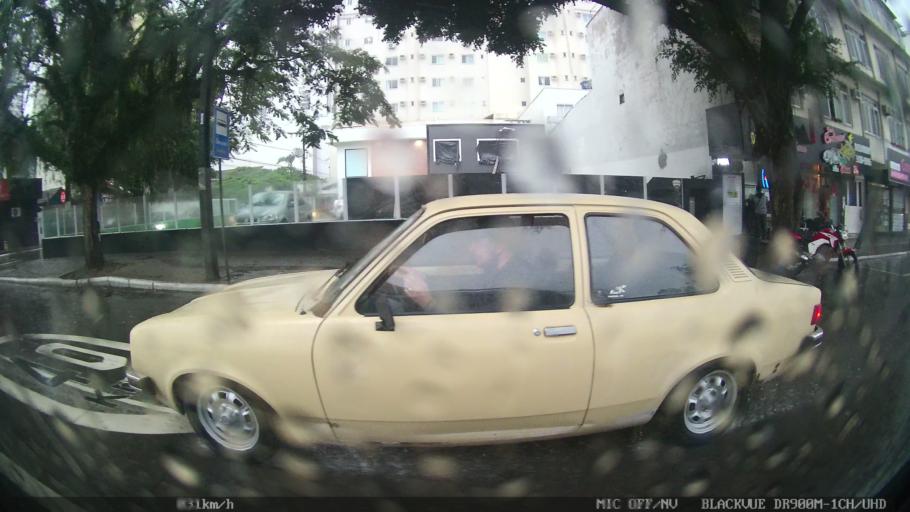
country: BR
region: Santa Catarina
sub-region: Balneario Camboriu
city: Balneario Camboriu
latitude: -26.9945
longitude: -48.6355
